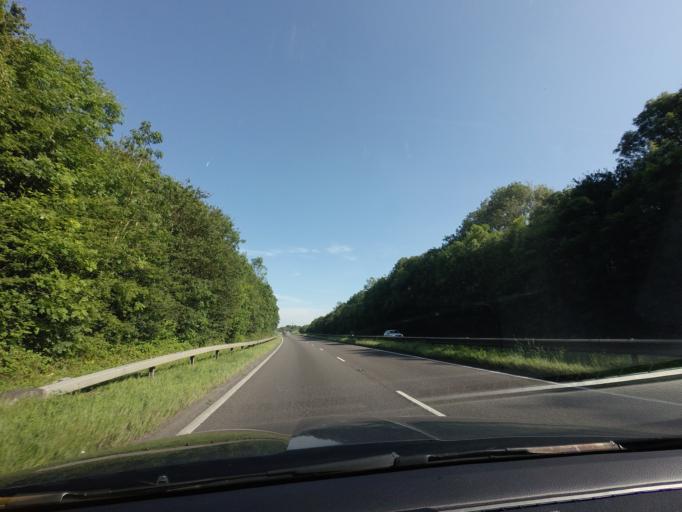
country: GB
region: England
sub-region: Derbyshire
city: Chesterfield
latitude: 53.2122
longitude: -1.3889
